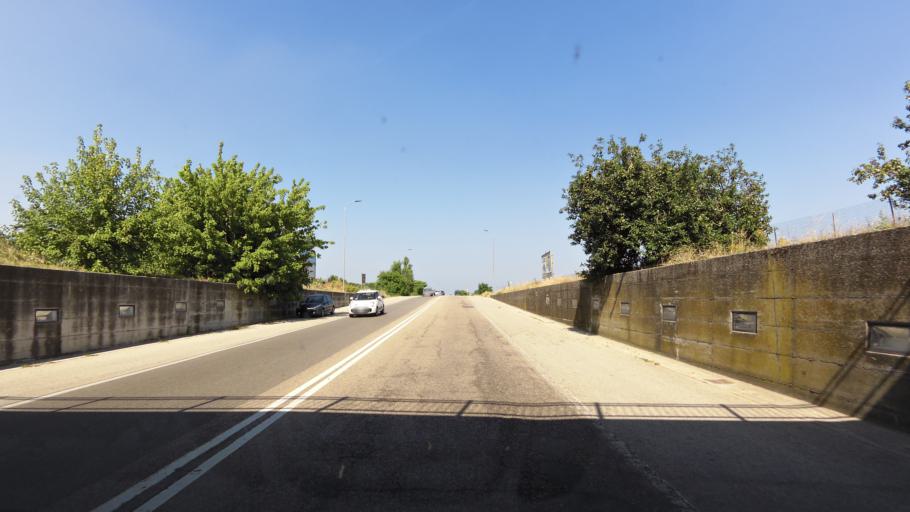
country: IT
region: Emilia-Romagna
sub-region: Provincia di Ravenna
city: Ravenna
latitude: 44.4021
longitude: 12.2173
